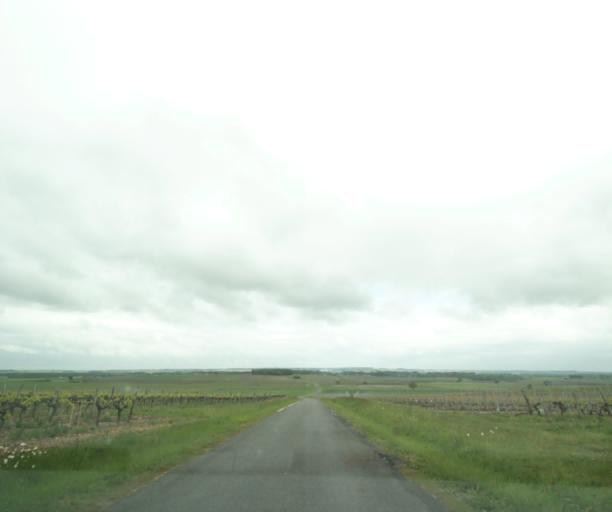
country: FR
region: Poitou-Charentes
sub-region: Departement de la Charente-Maritime
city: Perignac
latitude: 45.6644
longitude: -0.5010
